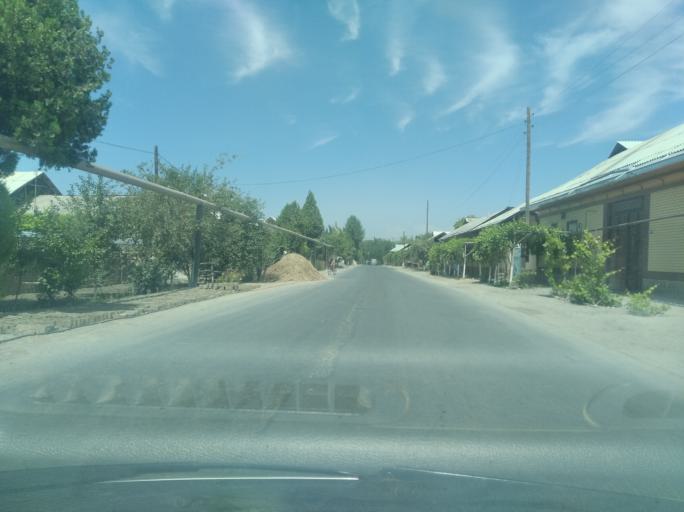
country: UZ
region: Andijon
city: Khujaobod
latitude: 40.6299
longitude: 72.4508
